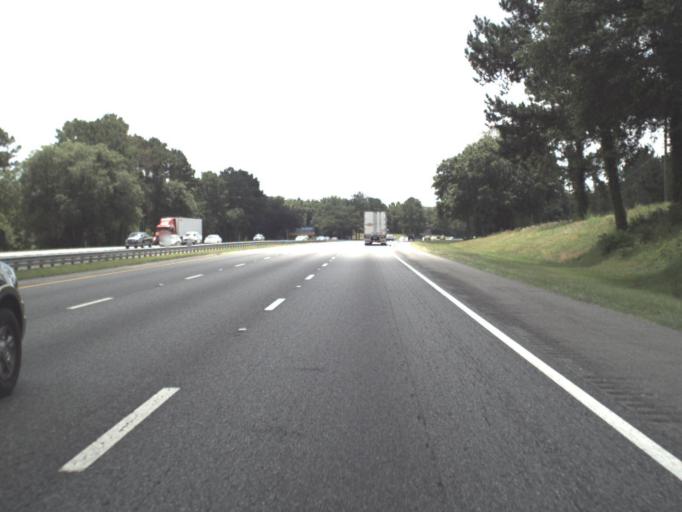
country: US
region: Florida
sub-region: Columbia County
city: Five Points
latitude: 30.2211
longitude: -82.7124
